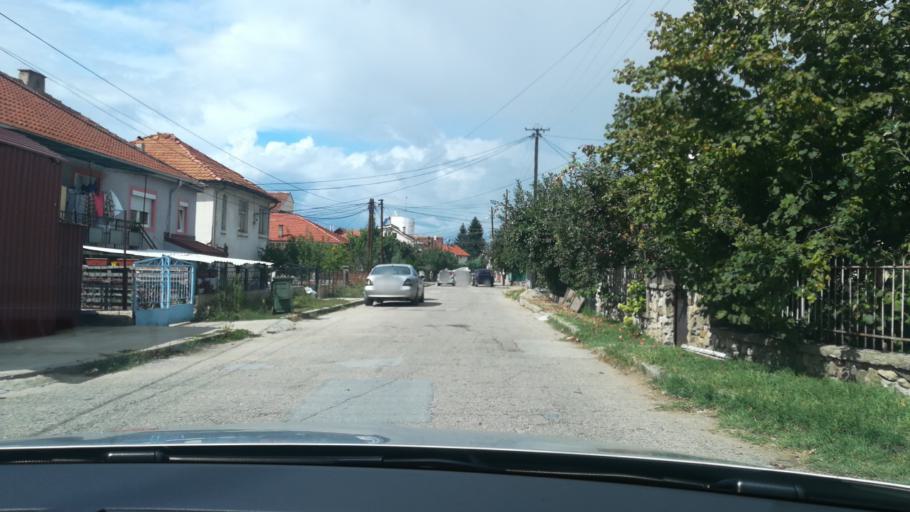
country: MK
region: Delcevo
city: Delcevo
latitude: 41.9643
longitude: 22.7774
